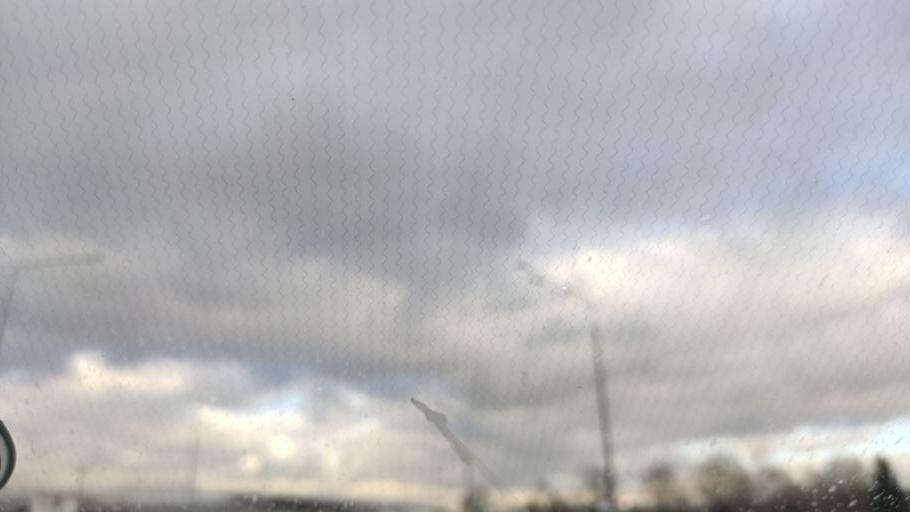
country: RU
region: Moskovskaya
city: Mosrentgen
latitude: 55.6024
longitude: 37.4174
